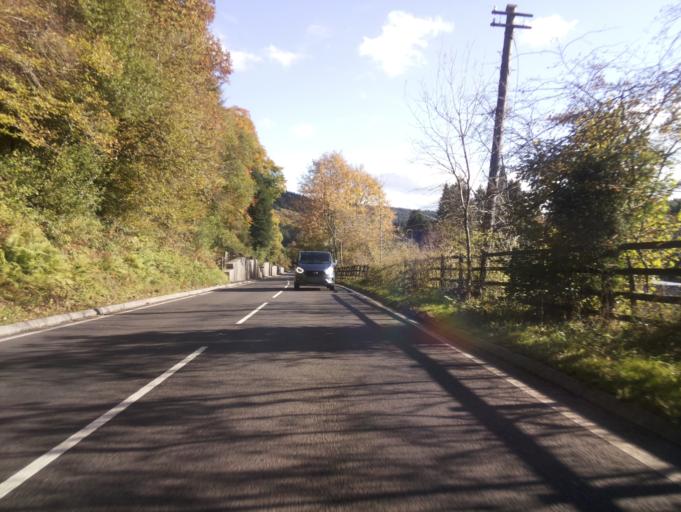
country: GB
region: Wales
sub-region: Rhondda Cynon Taf
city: Hirwaun
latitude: 51.8270
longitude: -3.4529
